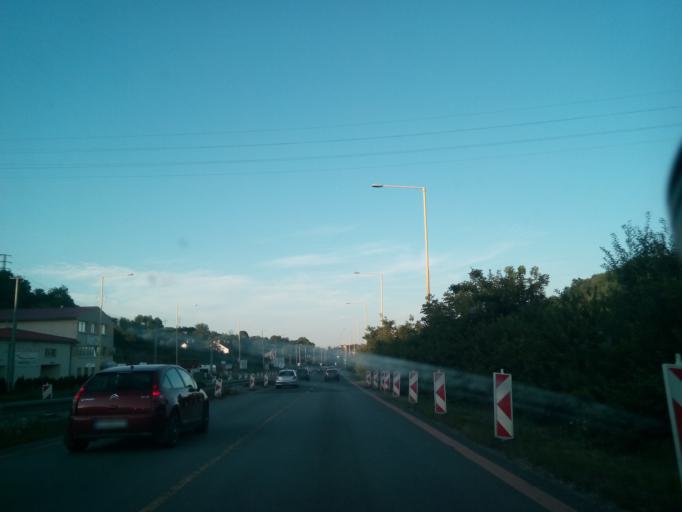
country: SK
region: Presovsky
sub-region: Okres Presov
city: Presov
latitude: 49.0001
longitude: 21.2080
